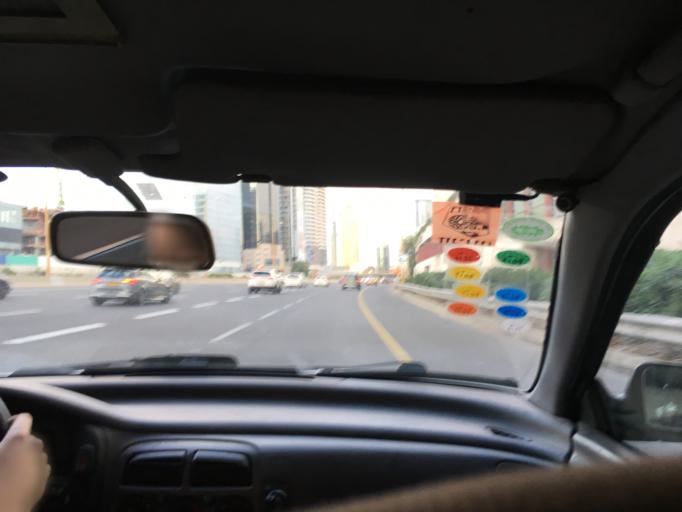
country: IL
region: Tel Aviv
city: Tel Aviv
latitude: 32.0757
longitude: 34.7942
